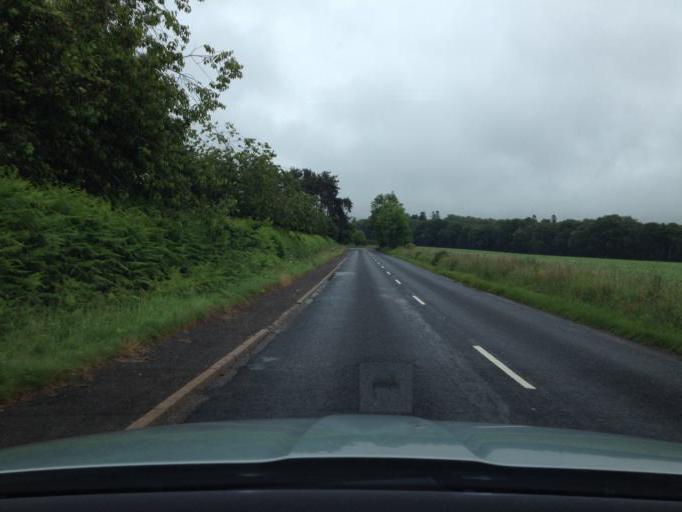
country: GB
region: Scotland
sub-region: Angus
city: Brechin
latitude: 56.8223
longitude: -2.6579
